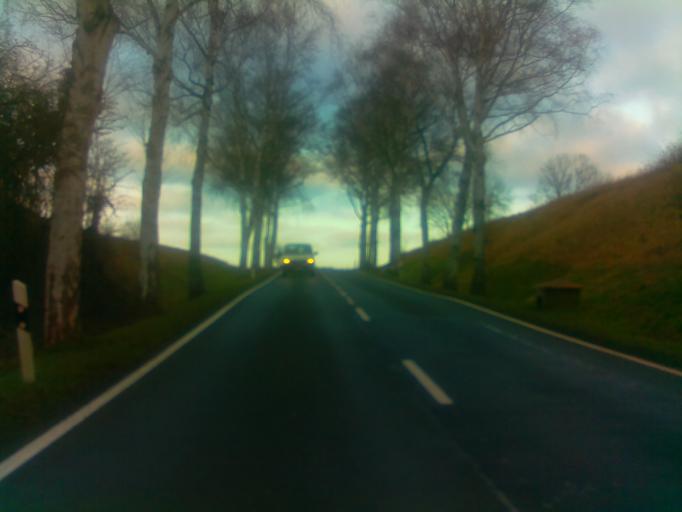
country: DE
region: Thuringia
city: Neustadt (Orla)
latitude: 50.7388
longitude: 11.7291
